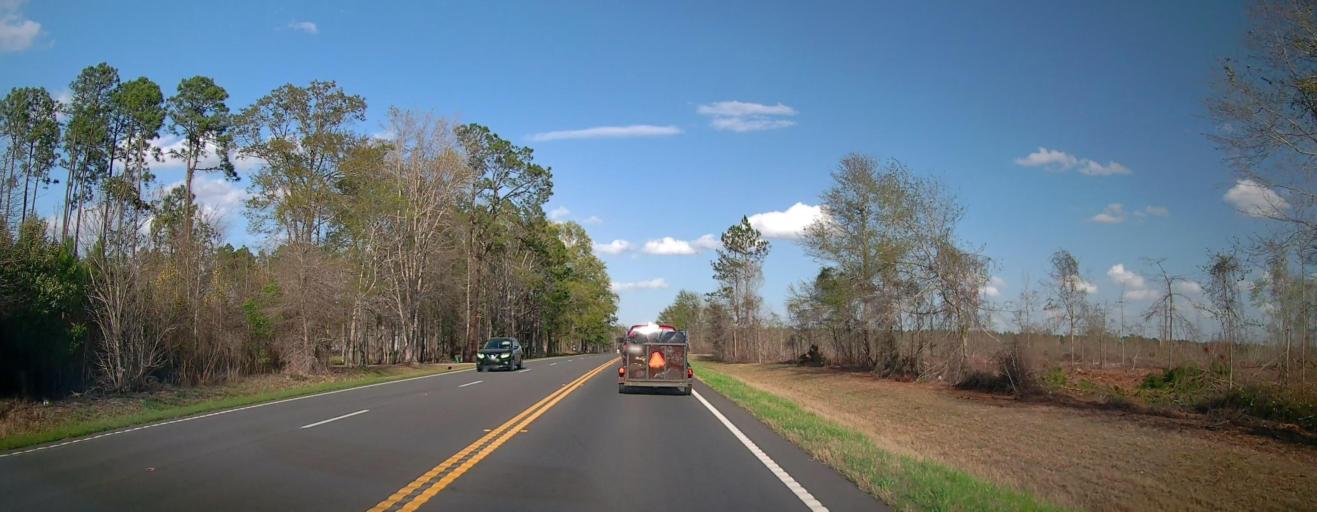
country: US
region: Georgia
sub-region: Montgomery County
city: Mount Vernon
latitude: 32.1920
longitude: -82.5181
